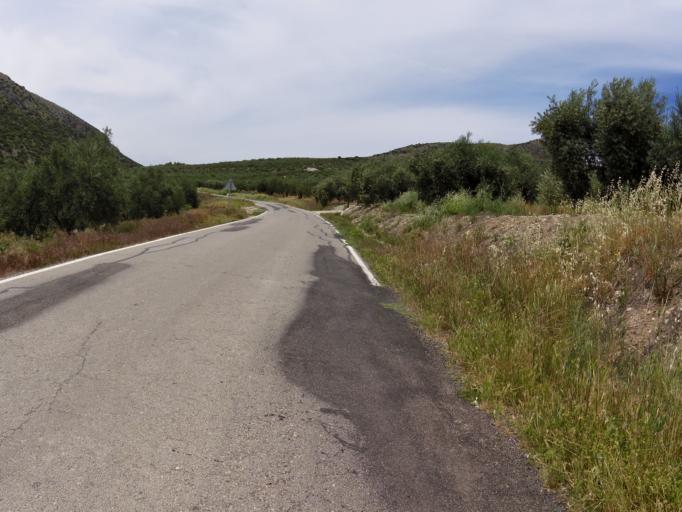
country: ES
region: Andalusia
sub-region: Province of Cordoba
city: Luque
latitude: 37.5190
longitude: -4.2224
